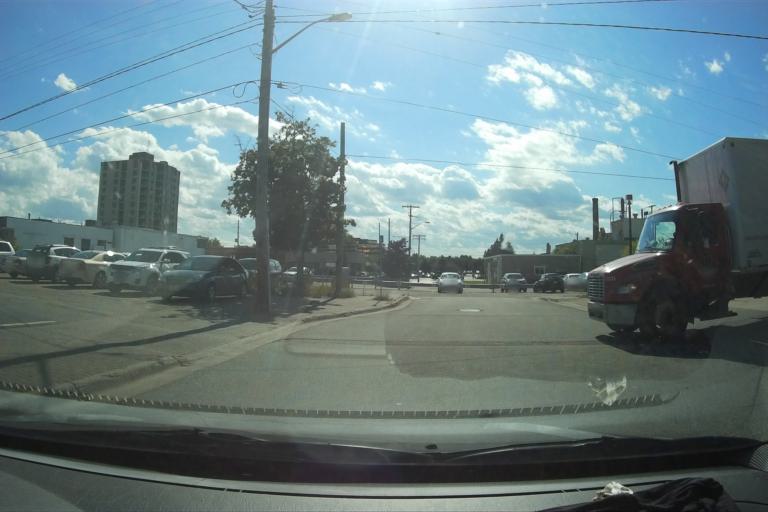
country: CA
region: Ontario
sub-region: Algoma
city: Sault Ste. Marie
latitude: 46.5095
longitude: -84.3309
